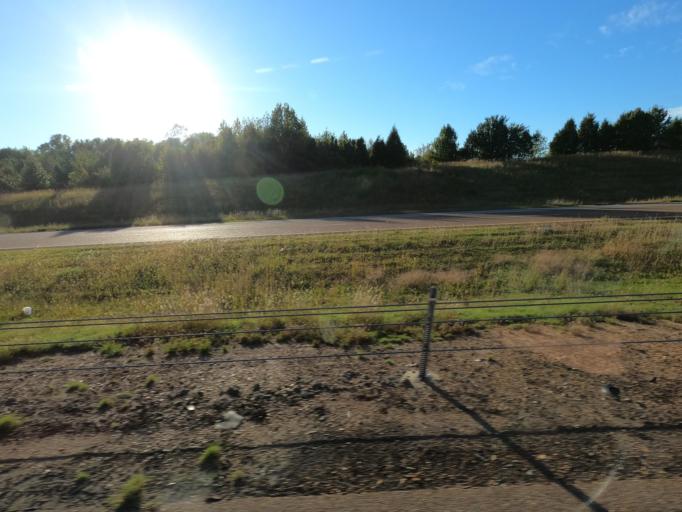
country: US
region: Tennessee
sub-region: Shelby County
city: Arlington
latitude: 35.2699
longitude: -89.6787
